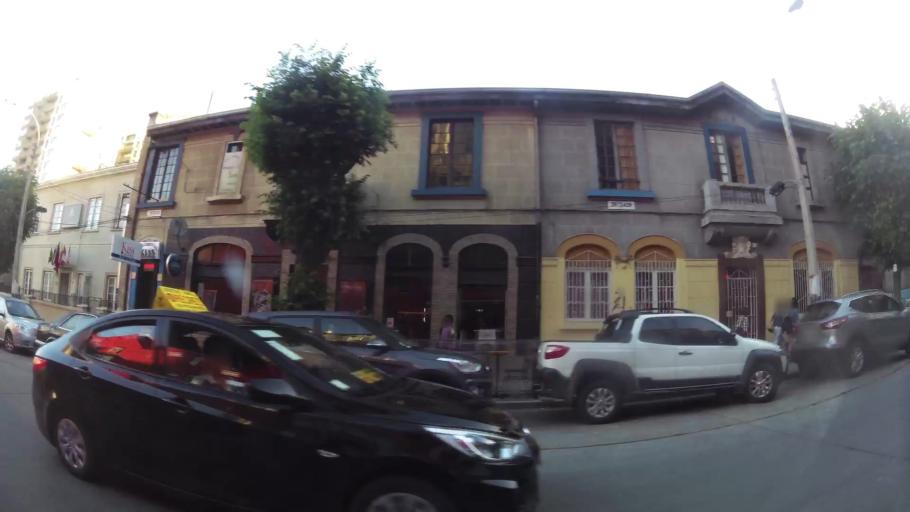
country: CL
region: Valparaiso
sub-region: Provincia de Valparaiso
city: Vina del Mar
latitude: -33.0237
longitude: -71.5621
